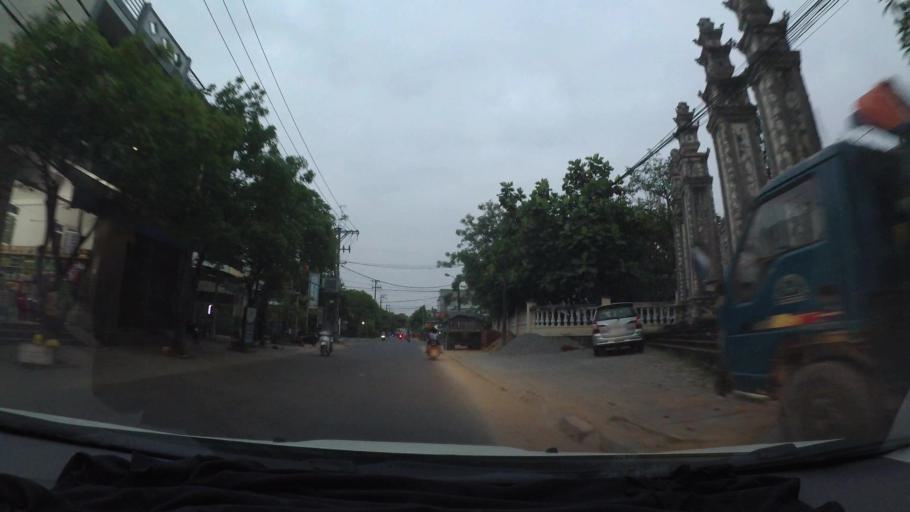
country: VN
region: Da Nang
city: Lien Chieu
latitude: 16.0506
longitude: 108.1703
